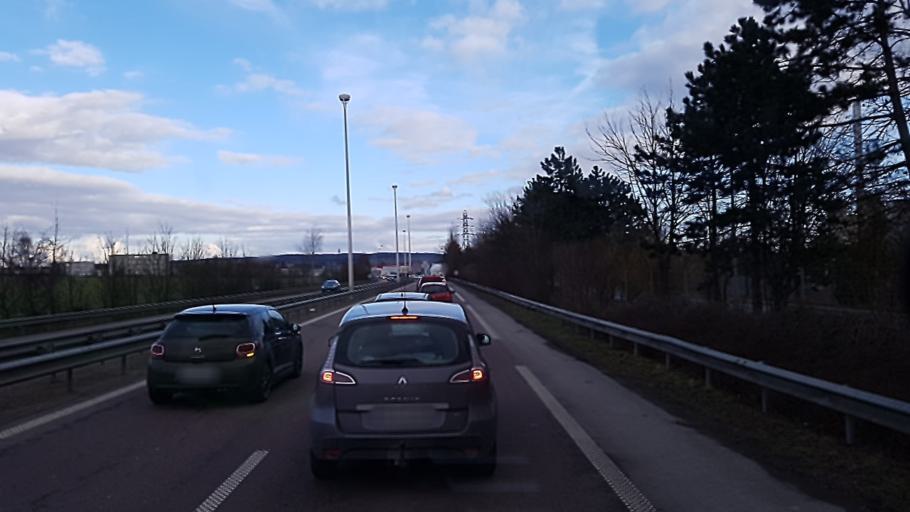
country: FR
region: Champagne-Ardenne
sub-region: Departement de la Marne
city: Betheny
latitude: 49.2729
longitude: 4.0619
